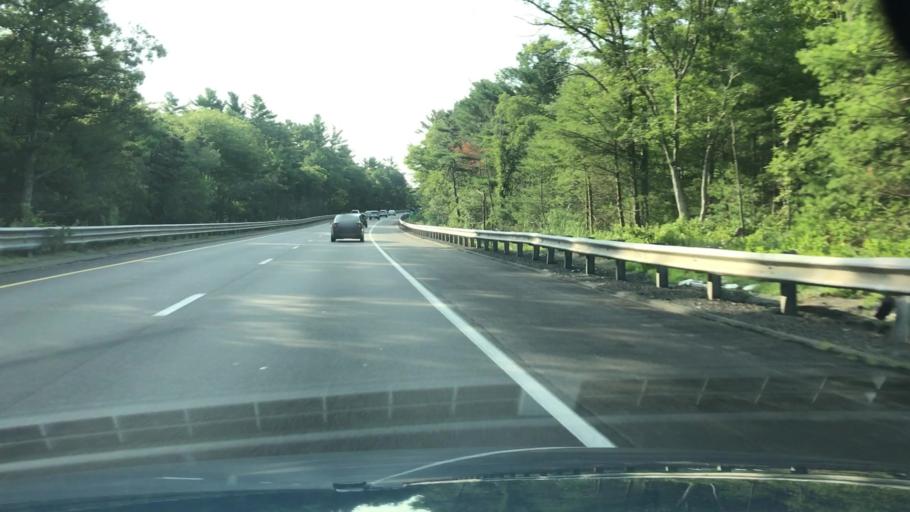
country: US
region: Massachusetts
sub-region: Plymouth County
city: Plymouth
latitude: 41.9272
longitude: -70.6338
